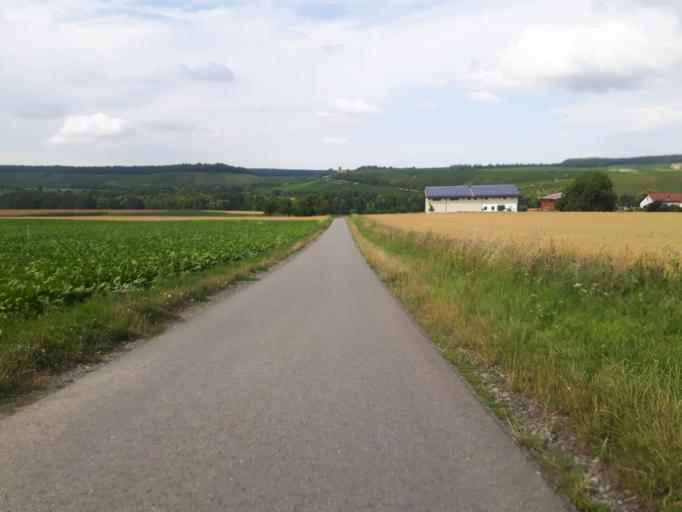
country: DE
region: Baden-Wuerttemberg
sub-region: Regierungsbezirk Stuttgart
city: Brackenheim
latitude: 49.0837
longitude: 9.0500
